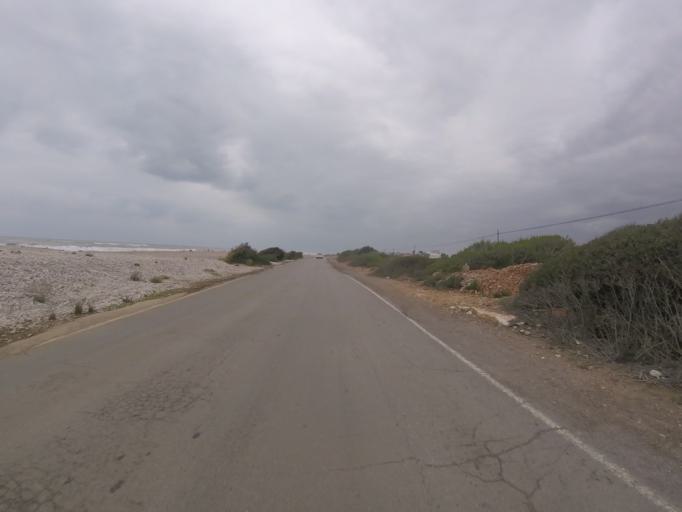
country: ES
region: Valencia
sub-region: Provincia de Castello
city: Alcoceber
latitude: 40.2173
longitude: 0.2672
